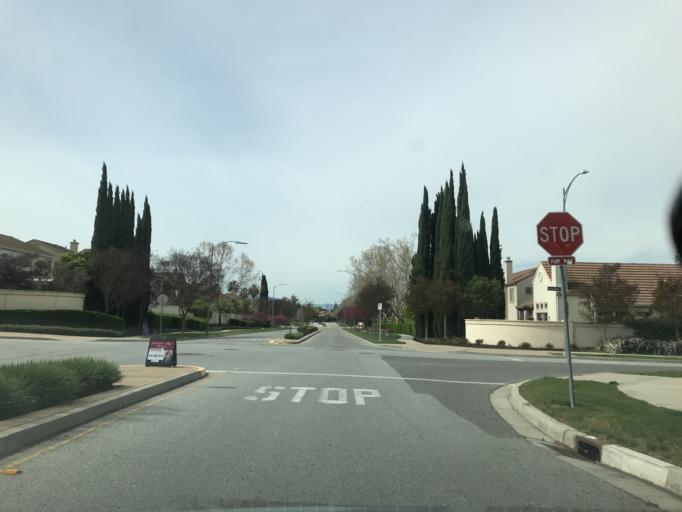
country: US
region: California
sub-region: Santa Clara County
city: Seven Trees
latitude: 37.3120
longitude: -121.7775
